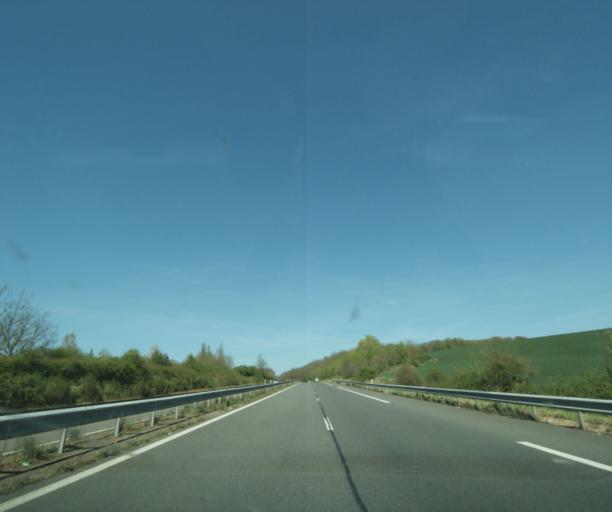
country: FR
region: Bourgogne
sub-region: Departement de la Nievre
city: Chaulgnes
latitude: 47.1074
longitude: 3.0702
